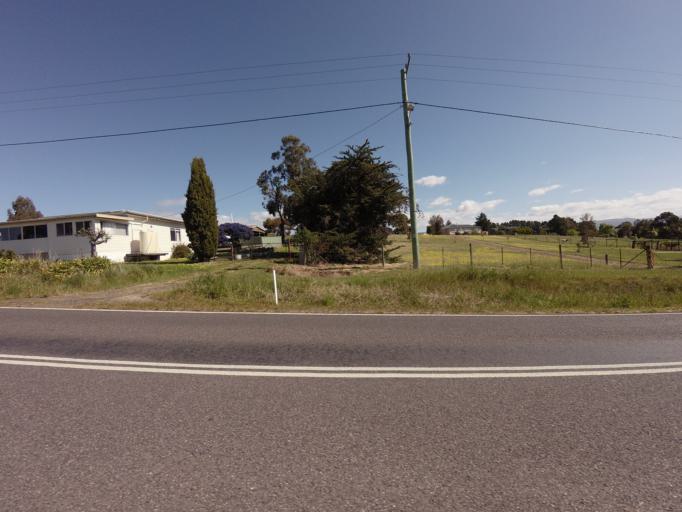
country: AU
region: Tasmania
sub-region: Derwent Valley
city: New Norfolk
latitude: -42.6972
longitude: 146.9418
